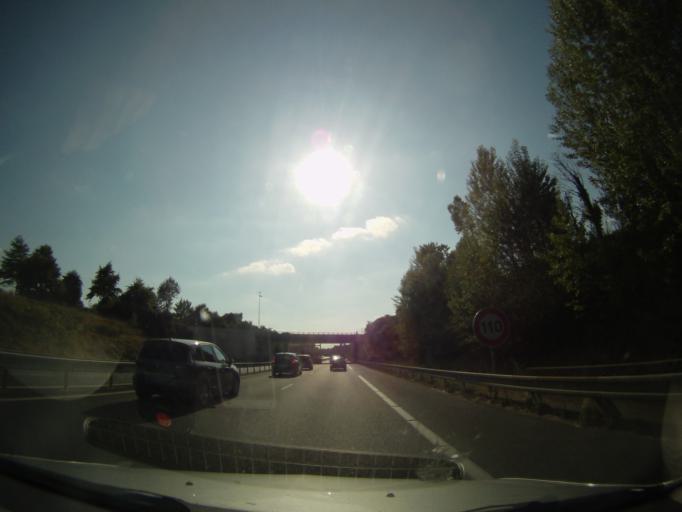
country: FR
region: Pays de la Loire
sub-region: Departement de la Loire-Atlantique
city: Carquefou
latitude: 47.2916
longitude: -1.4848
